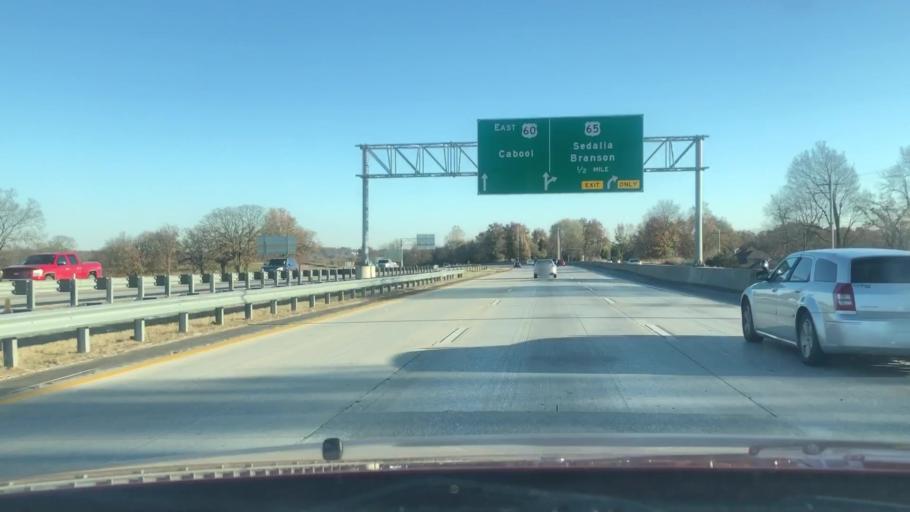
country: US
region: Missouri
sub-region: Greene County
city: Springfield
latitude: 37.1344
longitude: -93.2462
